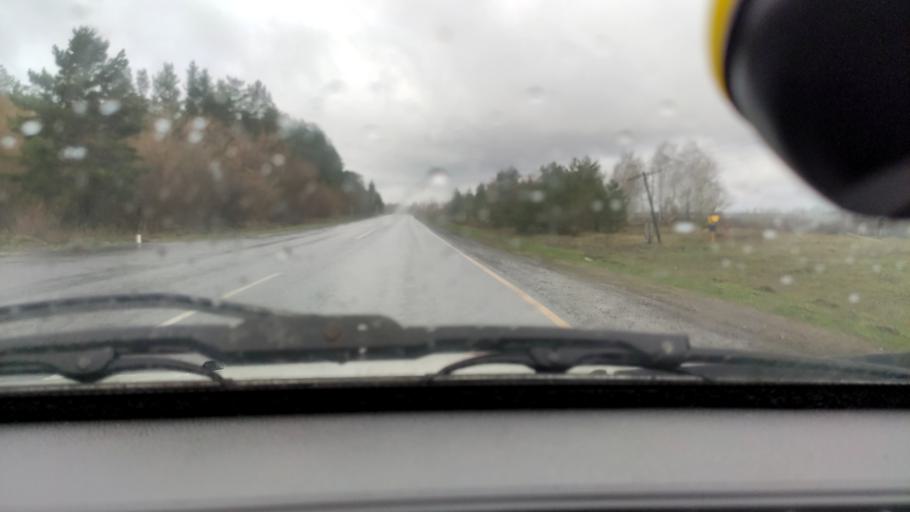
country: RU
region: Samara
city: Povolzhskiy
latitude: 53.6039
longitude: 49.6019
